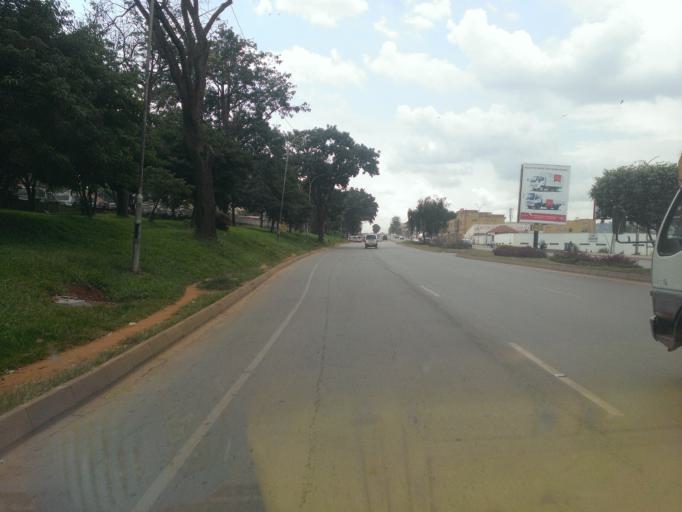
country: UG
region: Central Region
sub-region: Kampala District
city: Kampala
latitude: 0.3203
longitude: 32.5978
